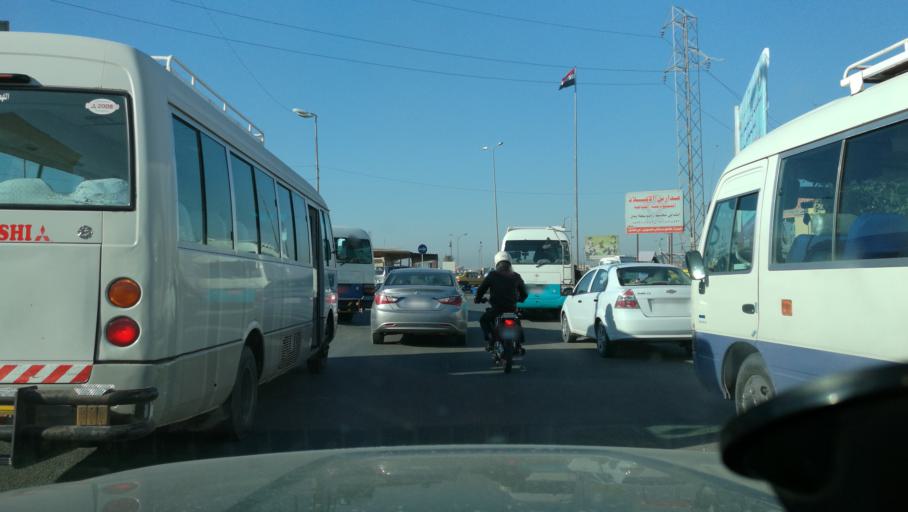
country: IQ
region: Basra Governorate
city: Al Basrah al Qadimah
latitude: 30.4843
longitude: 47.8046
